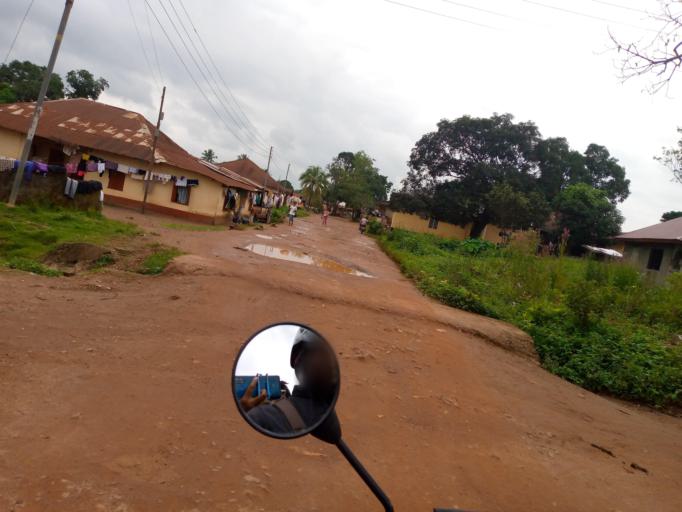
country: SL
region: Eastern Province
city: Kenema
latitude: 7.8633
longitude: -11.1940
